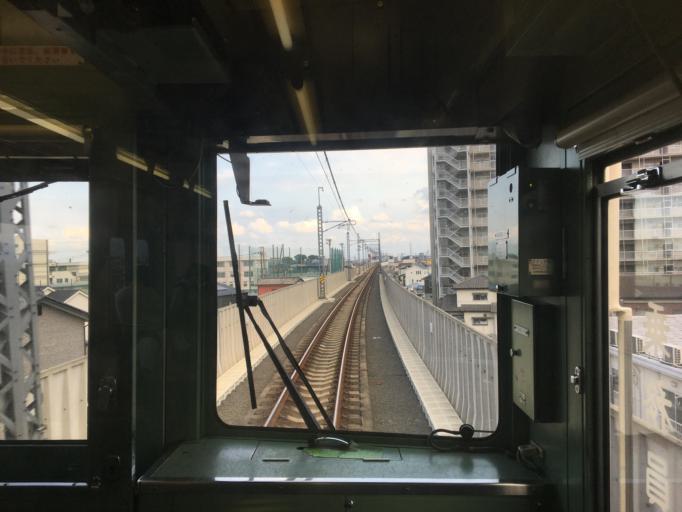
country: JP
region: Gunma
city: Isesaki
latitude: 36.3233
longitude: 139.1998
